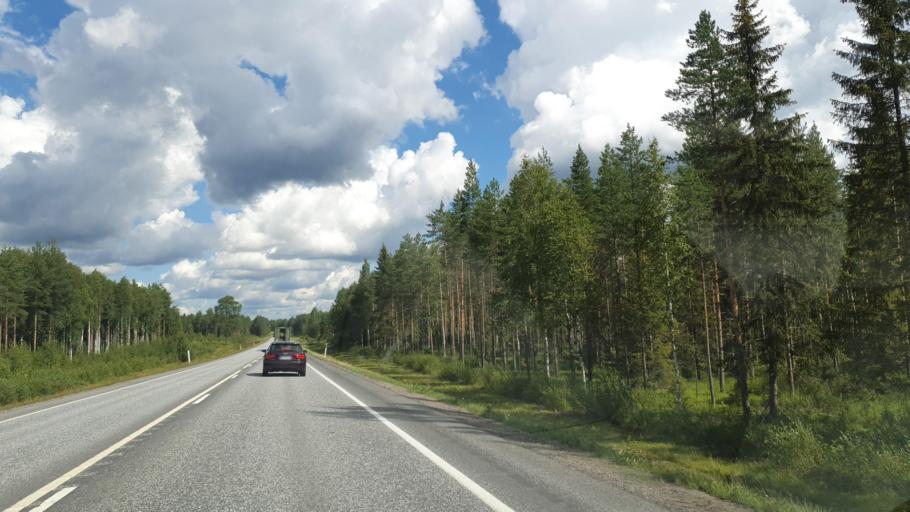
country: FI
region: Kainuu
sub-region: Kajaani
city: Kajaani
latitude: 64.1300
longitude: 27.4784
